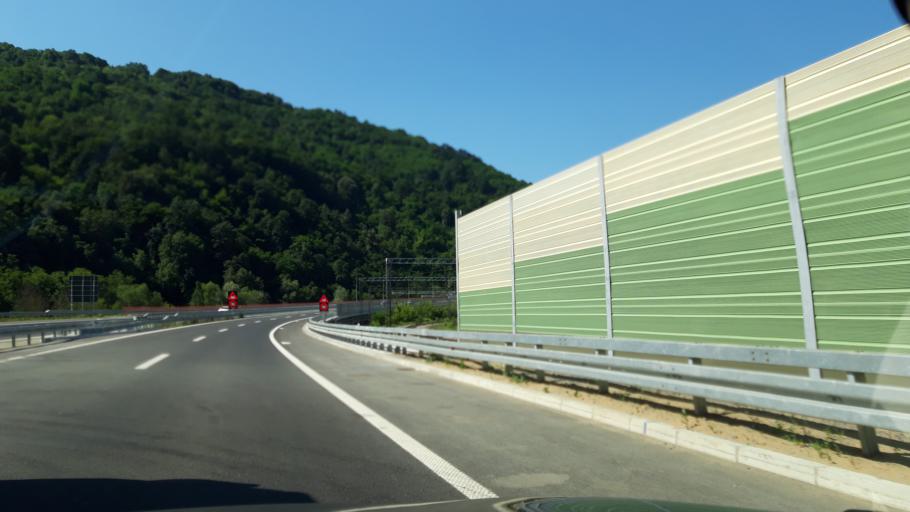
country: RS
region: Central Serbia
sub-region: Jablanicki Okrug
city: Vlasotince
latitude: 42.8299
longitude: 22.1285
